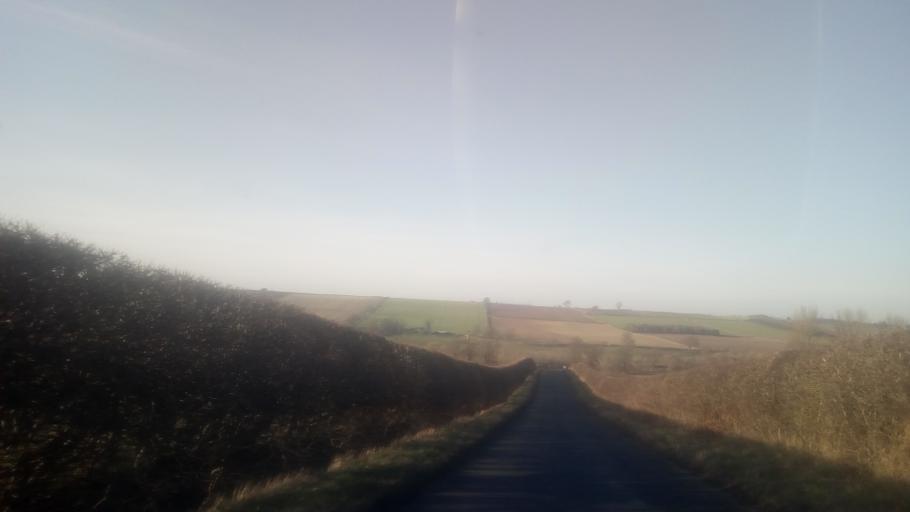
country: GB
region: Scotland
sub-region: The Scottish Borders
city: Jedburgh
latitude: 55.4929
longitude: -2.6011
